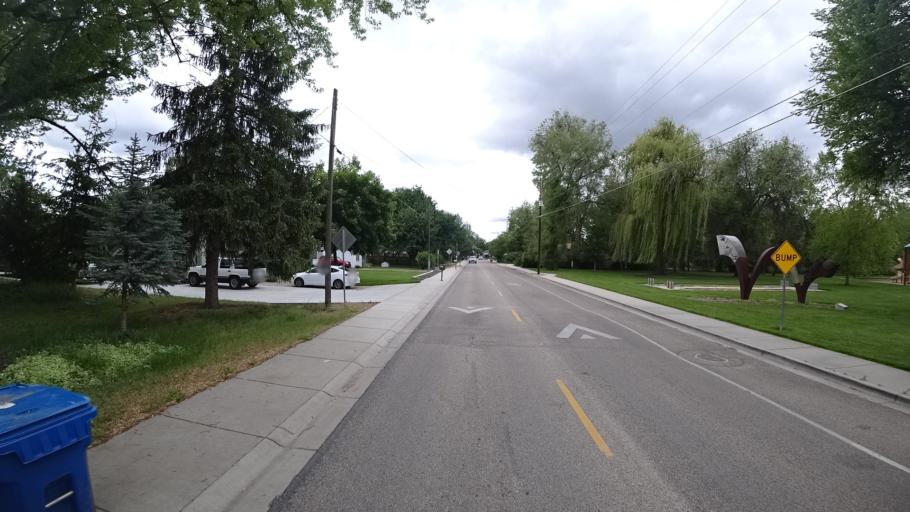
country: US
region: Idaho
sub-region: Ada County
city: Garden City
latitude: 43.6555
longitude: -116.2457
